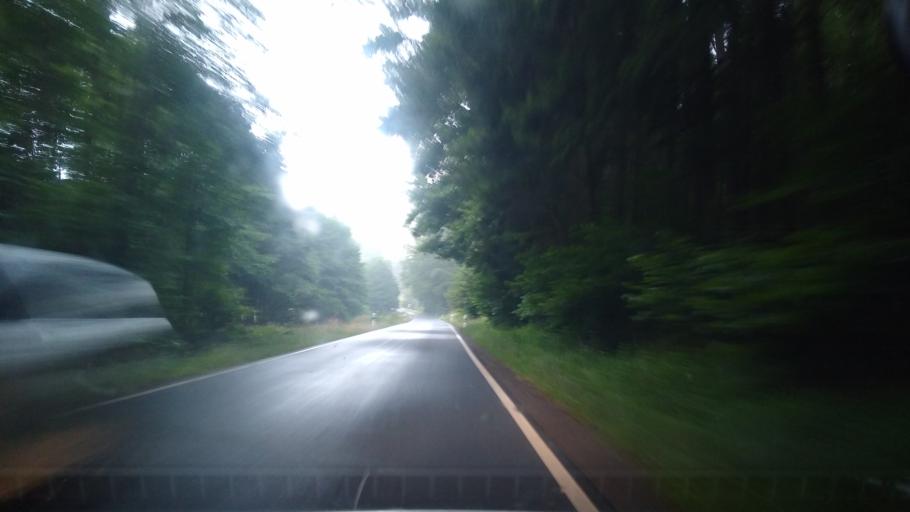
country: DE
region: Hesse
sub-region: Regierungsbezirk Darmstadt
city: Erbach
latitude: 49.6509
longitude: 8.9363
